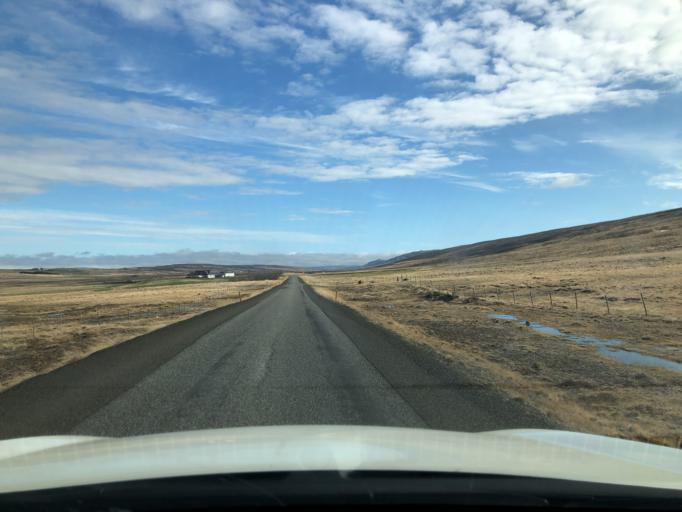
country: IS
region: West
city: Borgarnes
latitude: 65.0926
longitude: -21.7288
